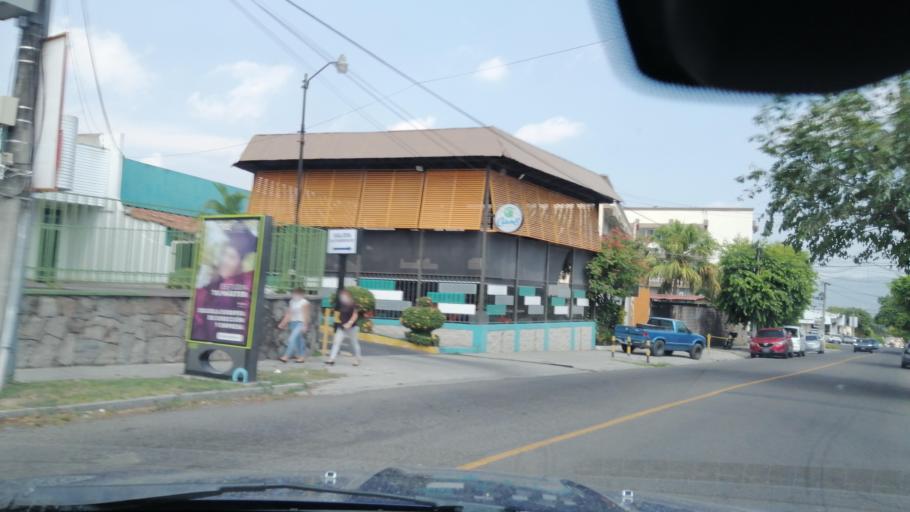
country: SV
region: La Libertad
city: Antiguo Cuscatlan
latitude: 13.7019
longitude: -89.2411
